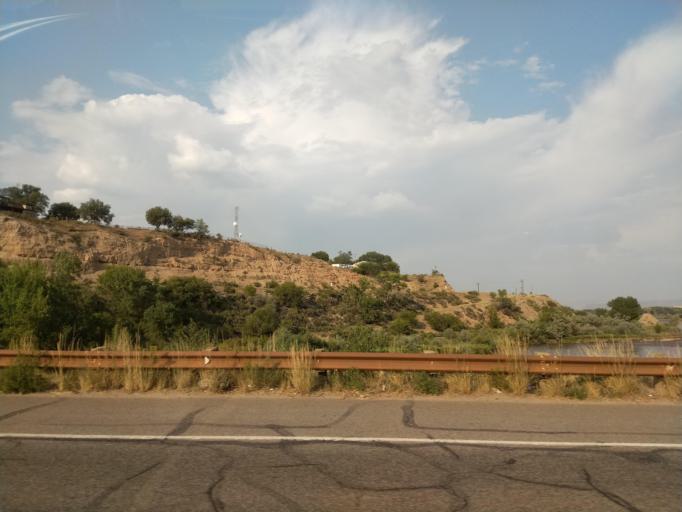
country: US
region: Colorado
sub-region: Garfield County
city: Rifle
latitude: 39.5277
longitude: -107.7794
